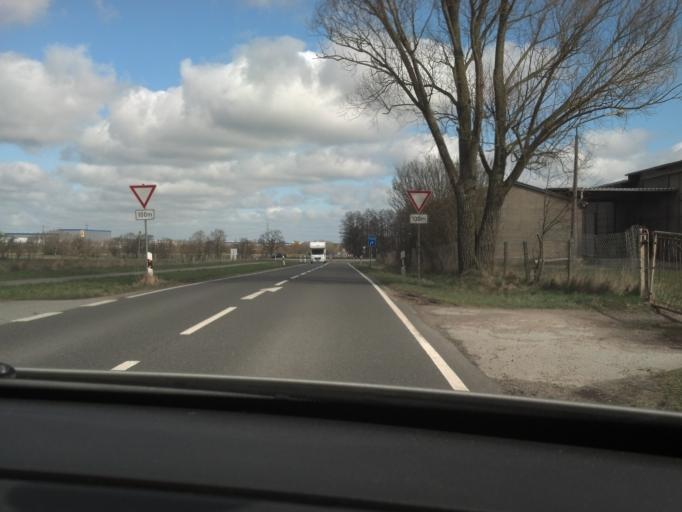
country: DE
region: Schleswig-Holstein
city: Hollenbek
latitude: 53.4990
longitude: 10.8358
